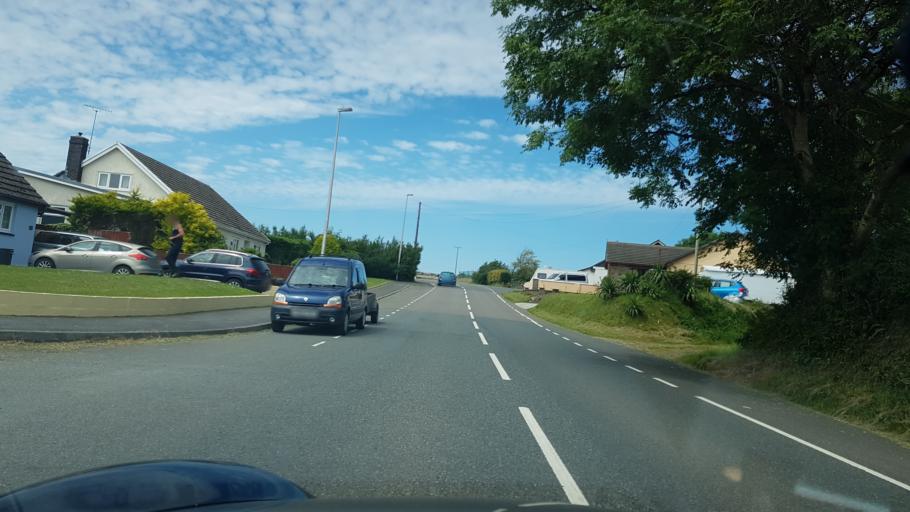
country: GB
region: Wales
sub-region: Carmarthenshire
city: Whitland
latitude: 51.7764
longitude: -4.6064
